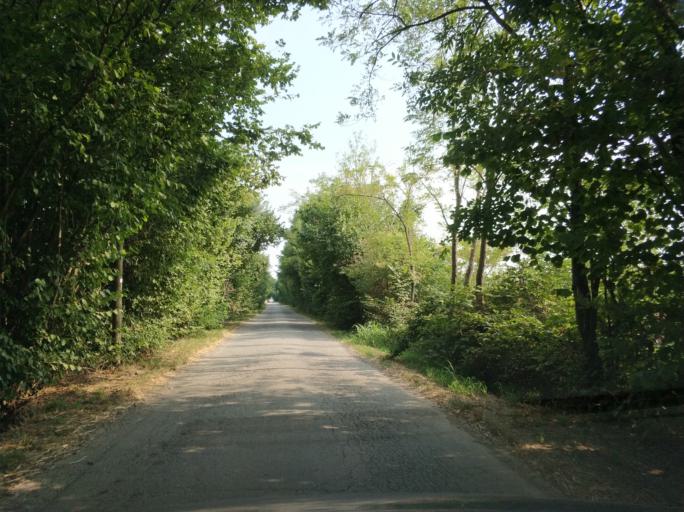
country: IT
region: Piedmont
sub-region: Provincia di Torino
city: Leini
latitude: 45.1897
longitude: 7.6864
